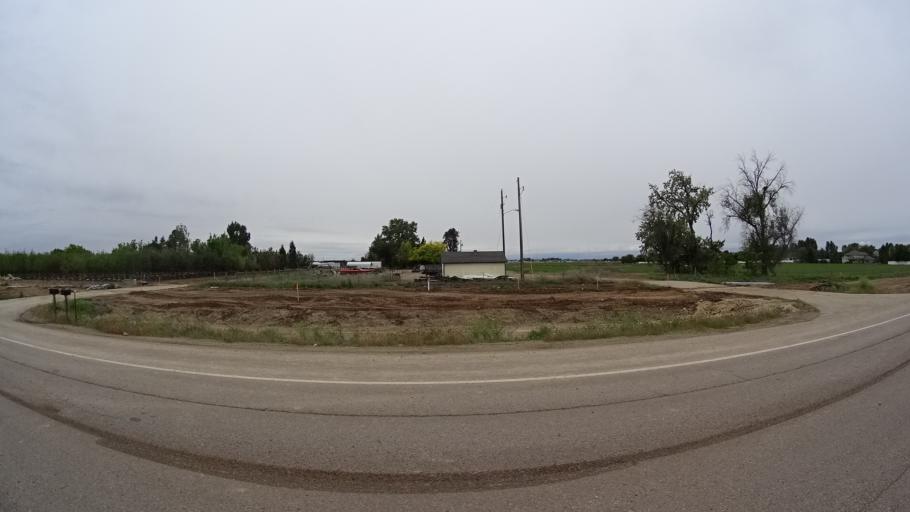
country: US
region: Idaho
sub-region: Ada County
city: Star
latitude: 43.6631
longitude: -116.4637
